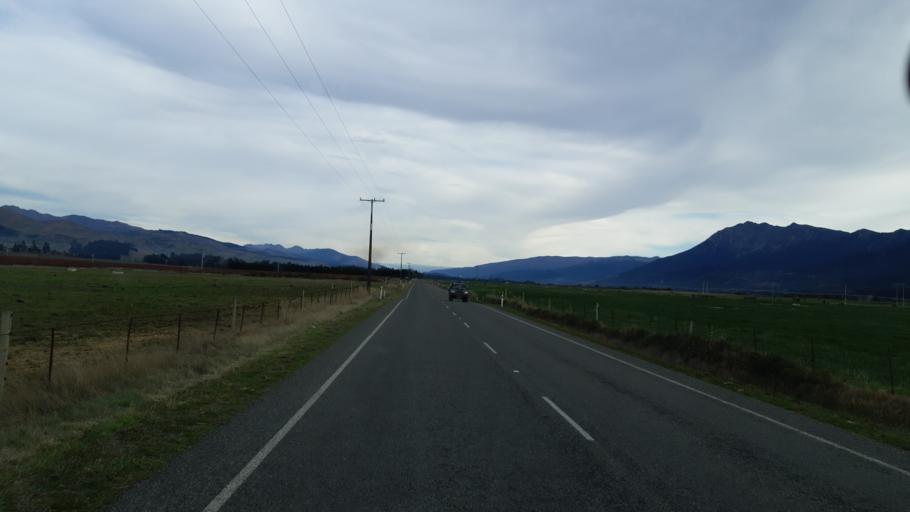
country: NZ
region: Tasman
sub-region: Tasman District
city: Richmond
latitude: -41.6117
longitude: 173.3929
